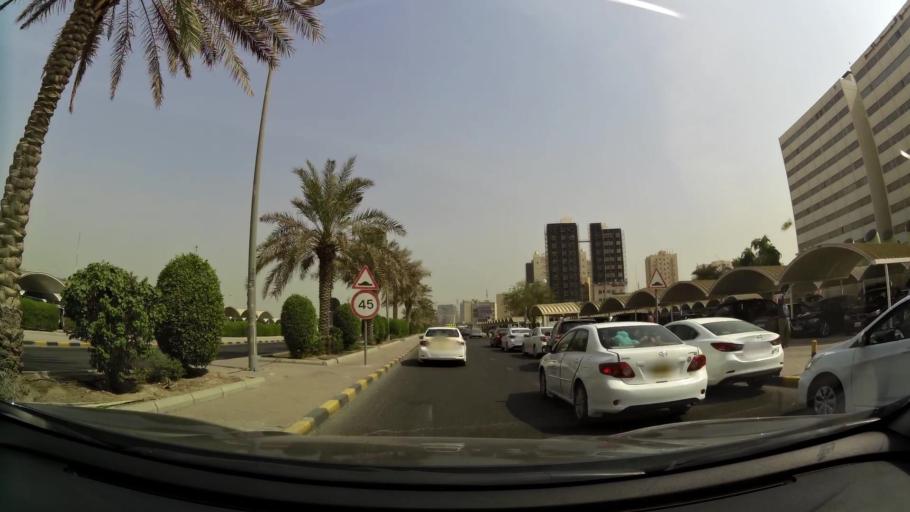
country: KW
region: Al Asimah
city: Ar Rabiyah
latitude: 29.3075
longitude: 47.9092
